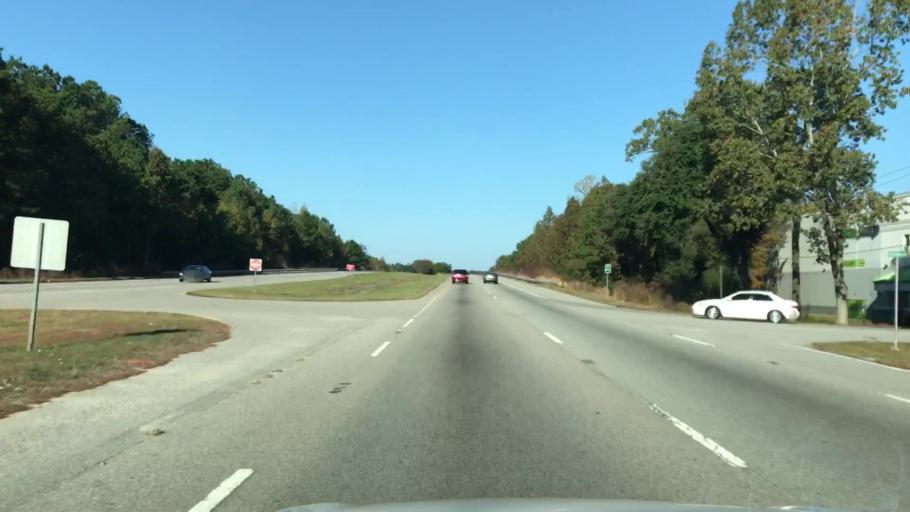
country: US
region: South Carolina
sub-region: Charleston County
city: Shell Point
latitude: 32.8216
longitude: -80.0713
